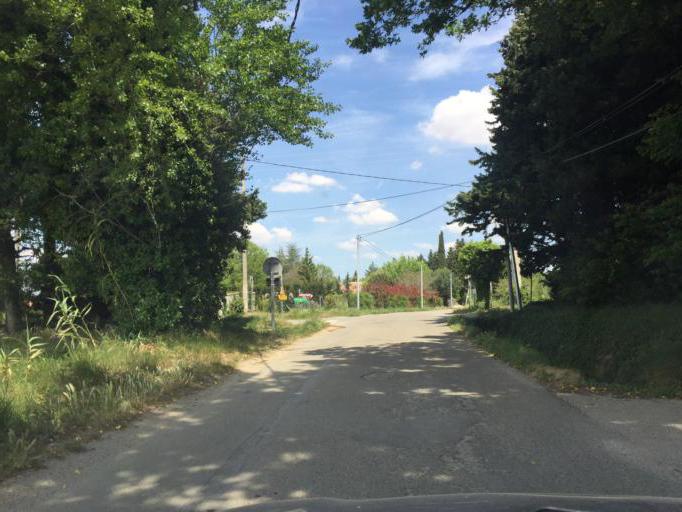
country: FR
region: Provence-Alpes-Cote d'Azur
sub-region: Departement du Vaucluse
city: Jonquieres
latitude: 44.1360
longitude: 4.9024
